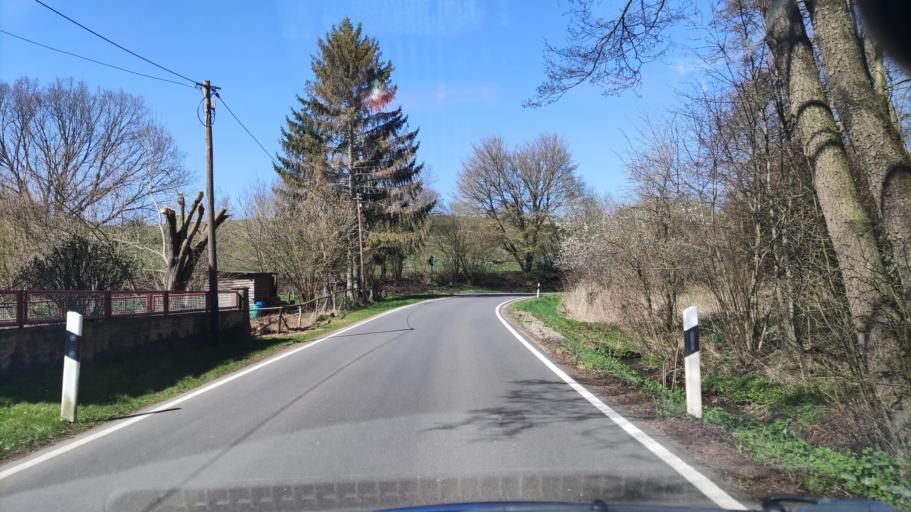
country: DE
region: Lower Saxony
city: Eimen
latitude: 51.9187
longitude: 9.7709
